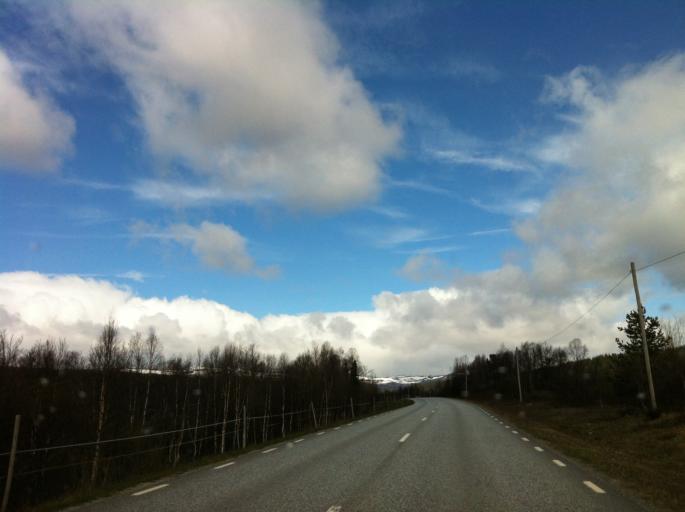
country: SE
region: Jaemtland
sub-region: Are Kommun
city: Are
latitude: 62.5900
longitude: 12.5513
